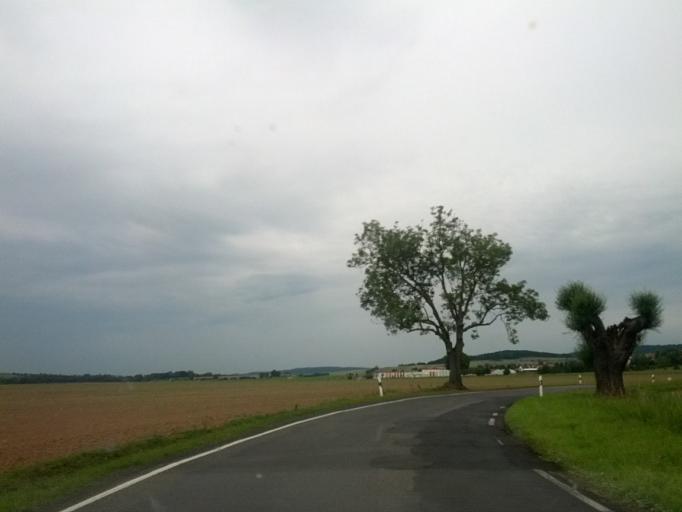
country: DE
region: Thuringia
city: Bad Salzungen
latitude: 50.8523
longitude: 10.2497
